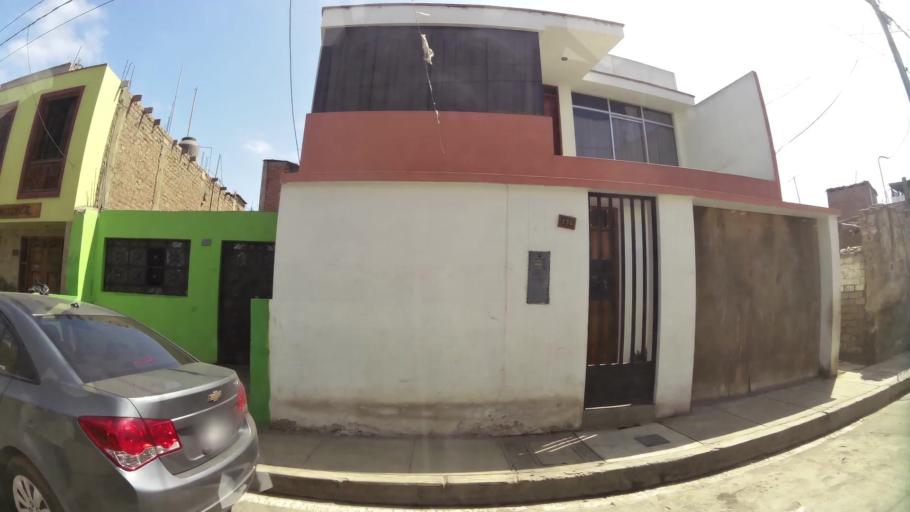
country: PE
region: Lima
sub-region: Provincia de Canete
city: Mala
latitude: -12.6531
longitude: -76.6354
